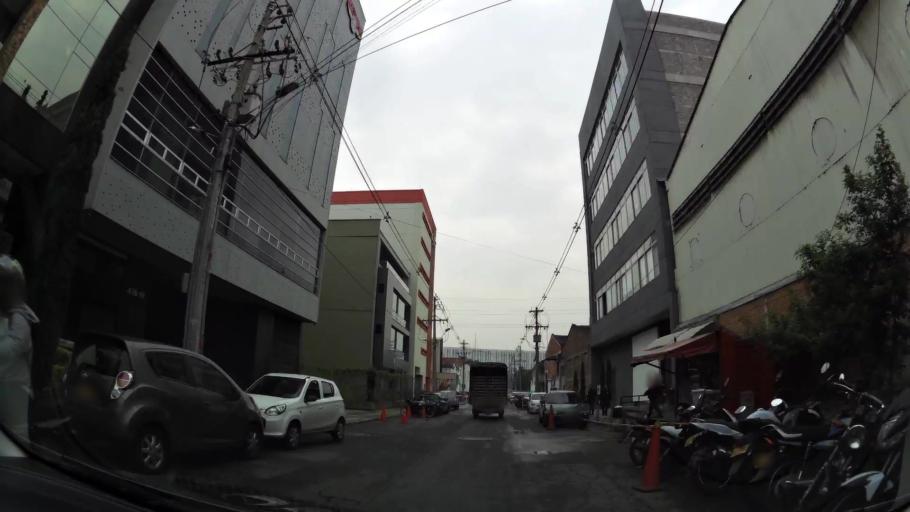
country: CO
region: Antioquia
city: Medellin
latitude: 6.2252
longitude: -75.5709
